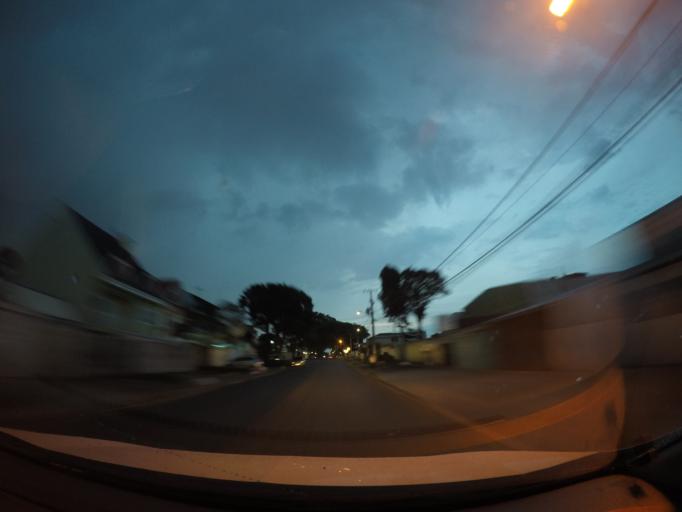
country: BR
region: Parana
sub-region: Sao Jose Dos Pinhais
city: Sao Jose dos Pinhais
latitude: -25.5133
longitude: -49.2277
